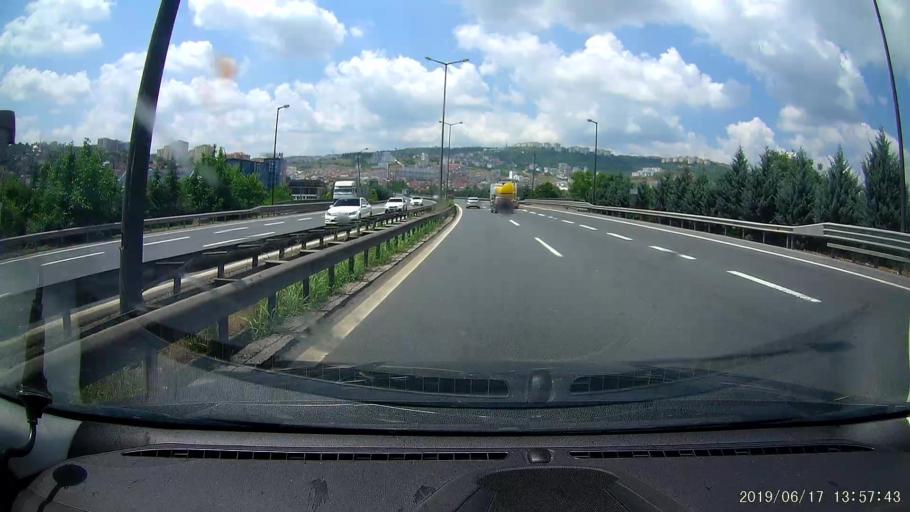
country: TR
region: Kocaeli
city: Kullar
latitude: 40.7835
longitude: 29.9750
